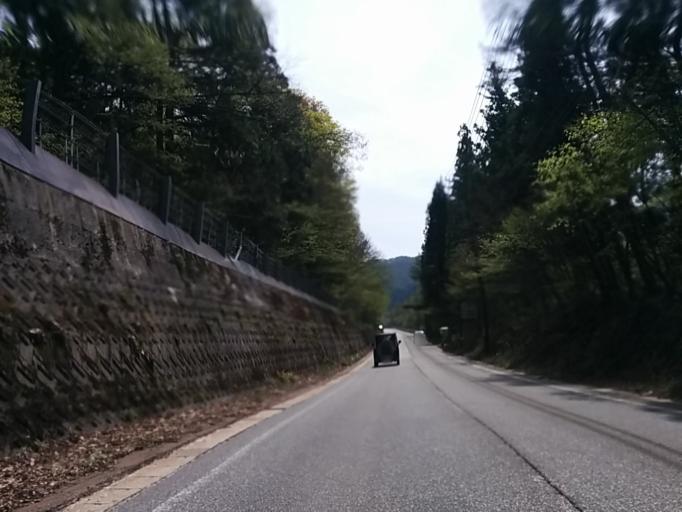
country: JP
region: Gifu
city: Takayama
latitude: 36.2155
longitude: 137.5441
